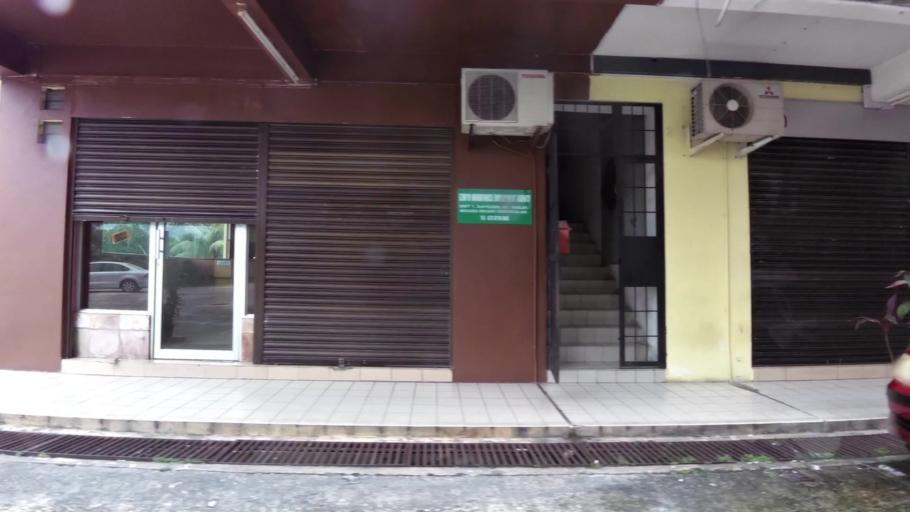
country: BN
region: Brunei and Muara
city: Bandar Seri Begawan
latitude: 4.9028
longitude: 114.9246
